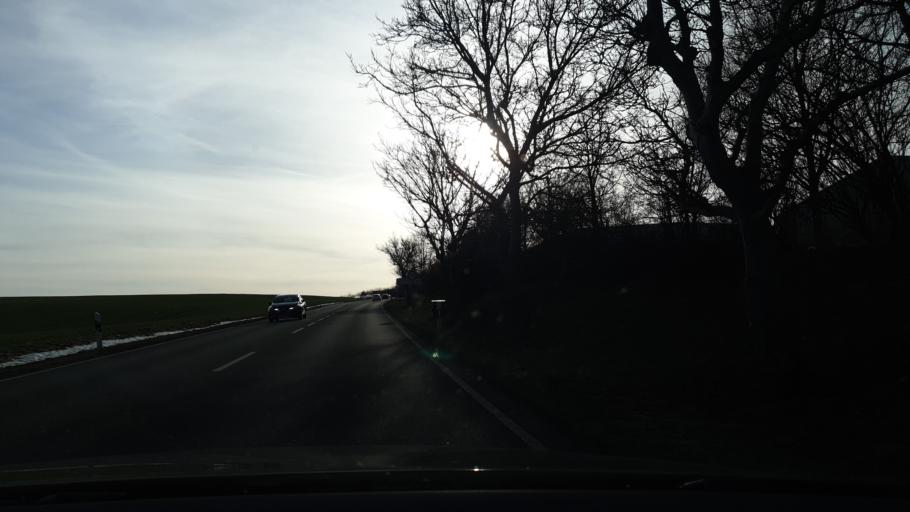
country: DE
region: Thuringia
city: Triebes
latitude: 50.6780
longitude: 12.0137
